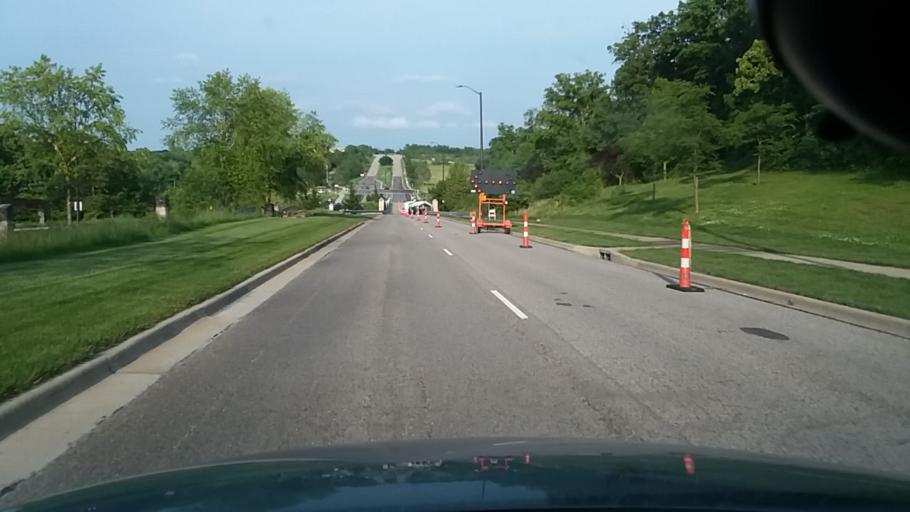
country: US
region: Kansas
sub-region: Johnson County
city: Lenexa
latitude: 38.9558
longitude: -94.8032
